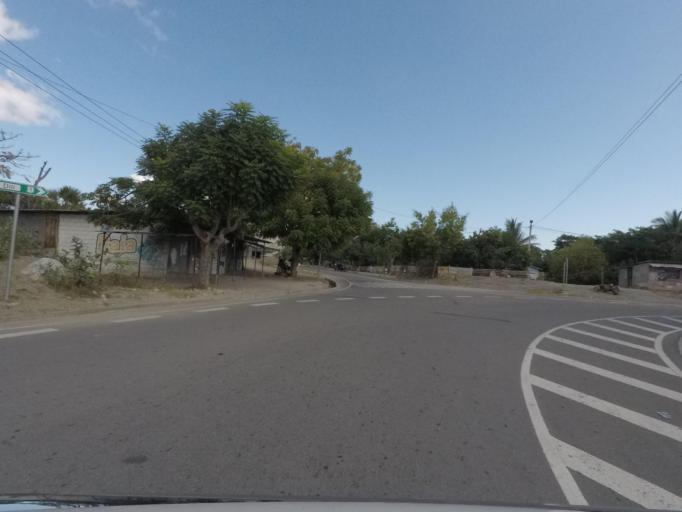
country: TL
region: Manatuto
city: Manatuto
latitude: -8.5185
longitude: 126.0072
